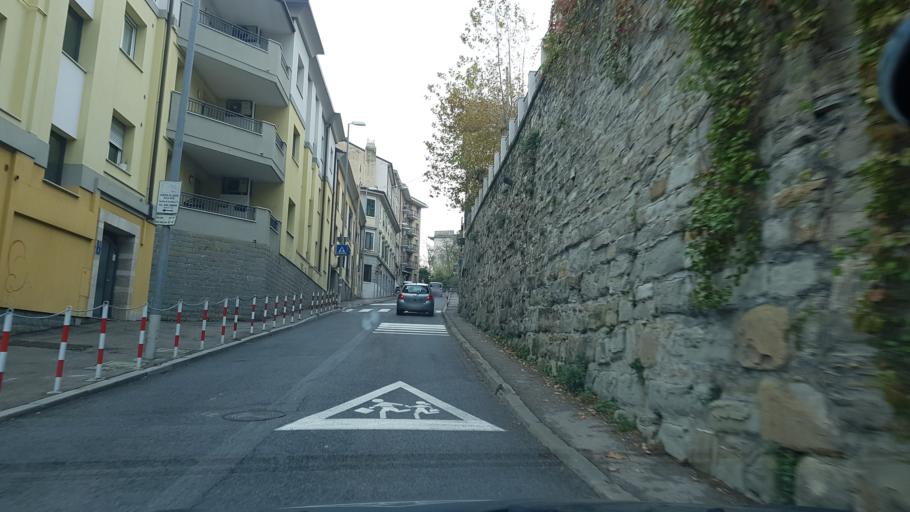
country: IT
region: Friuli Venezia Giulia
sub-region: Provincia di Trieste
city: Villa Opicina
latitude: 45.6652
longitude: 13.7686
